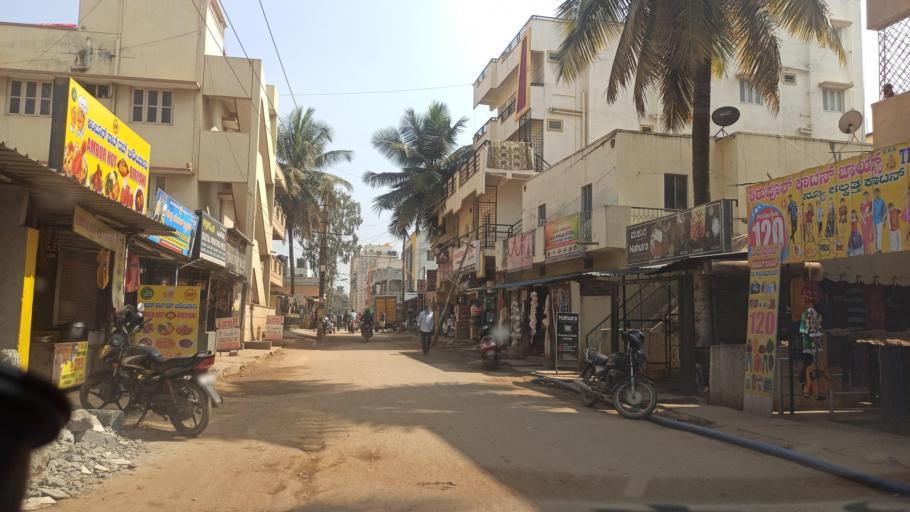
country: IN
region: Karnataka
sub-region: Bangalore Urban
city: Bangalore
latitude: 12.9480
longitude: 77.7058
